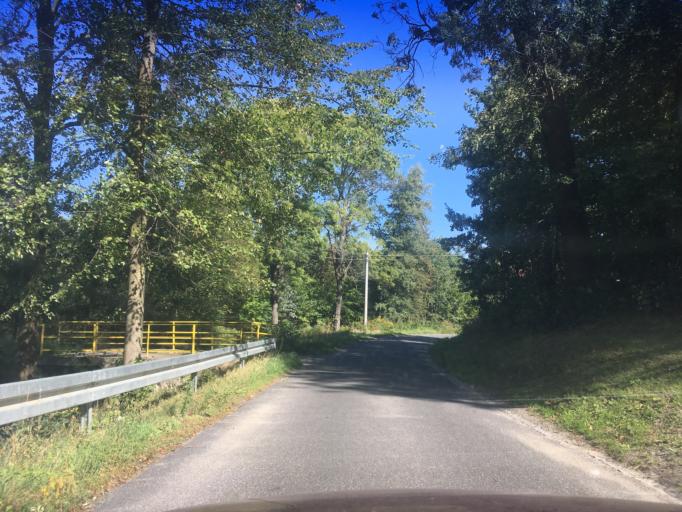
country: PL
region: Lower Silesian Voivodeship
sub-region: Powiat lubanski
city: Lesna
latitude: 51.0213
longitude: 15.2123
